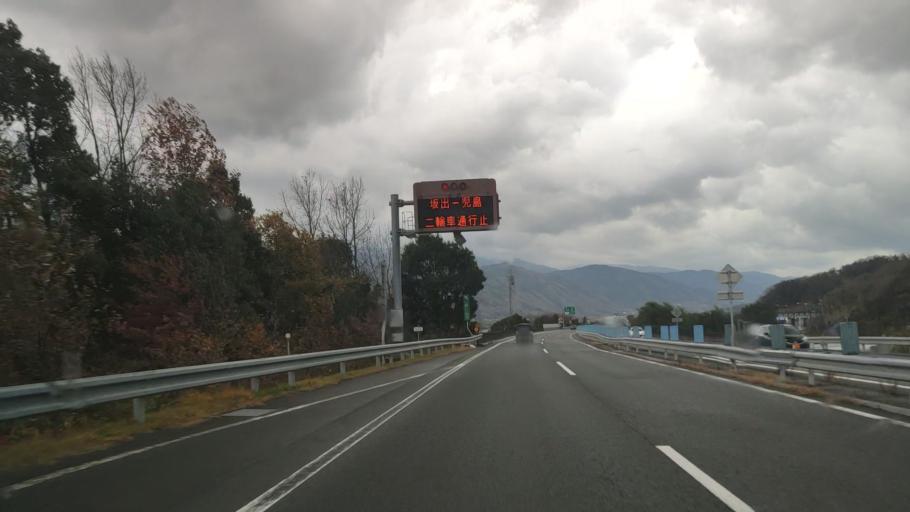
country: JP
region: Tokushima
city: Wakimachi
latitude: 34.0596
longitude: 134.0541
